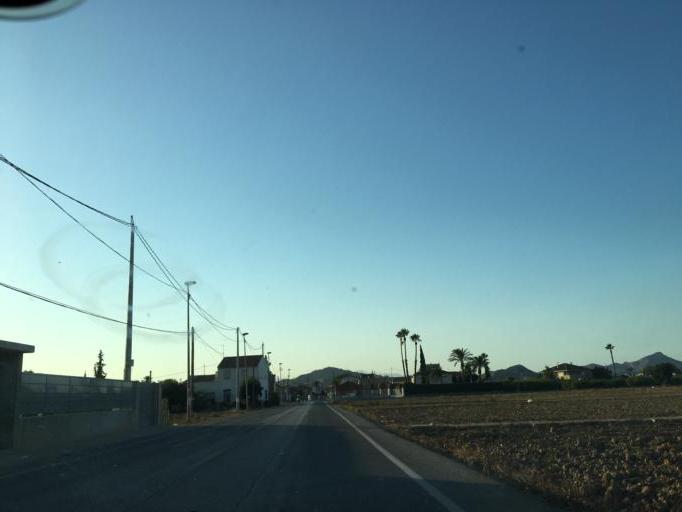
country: ES
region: Murcia
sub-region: Murcia
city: Murcia
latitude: 38.0039
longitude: -1.0778
